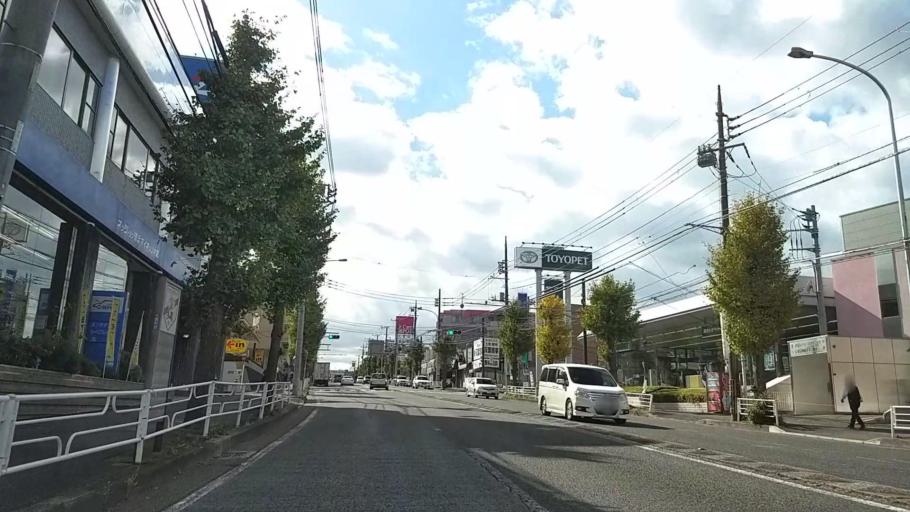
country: JP
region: Kanagawa
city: Yokohama
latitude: 35.4888
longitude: 139.6054
